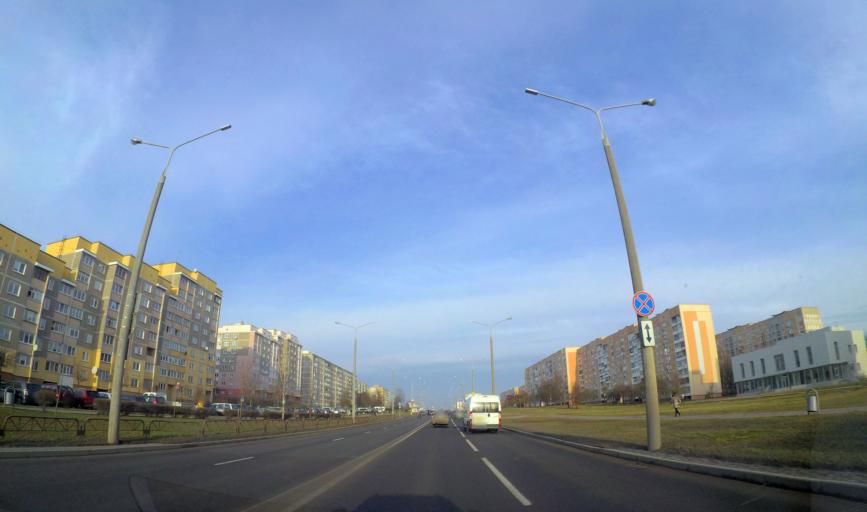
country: BY
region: Grodnenskaya
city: Hrodna
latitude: 53.6606
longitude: 23.7825
